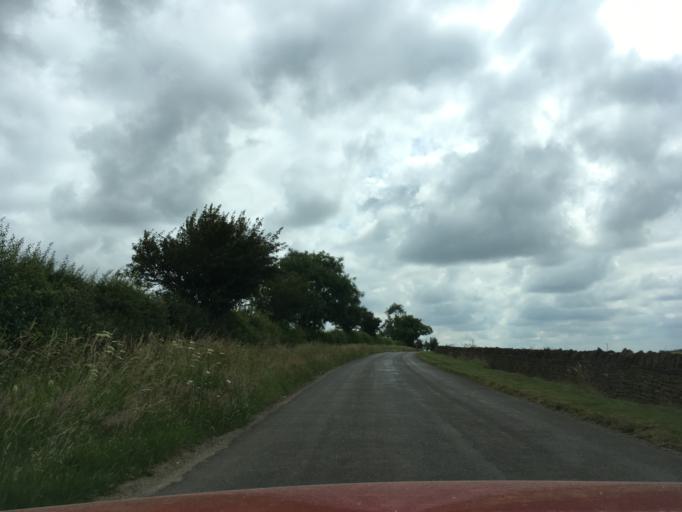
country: GB
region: England
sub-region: Oxfordshire
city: Chipping Norton
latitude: 51.9255
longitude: -1.5598
